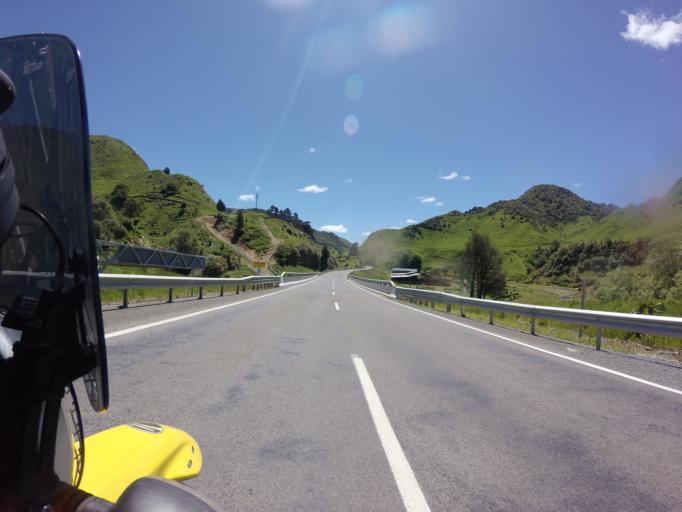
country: NZ
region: Bay of Plenty
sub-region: Opotiki District
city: Opotiki
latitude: -38.3802
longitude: 177.4701
